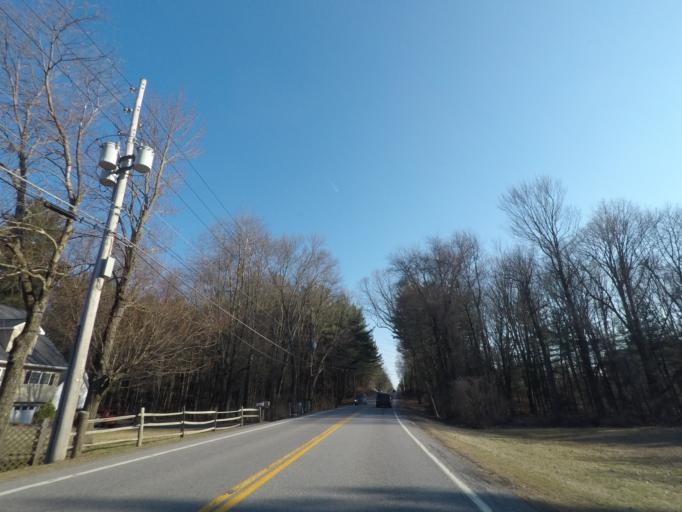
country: US
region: New York
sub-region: Schenectady County
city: Niskayuna
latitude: 42.8324
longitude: -73.7757
